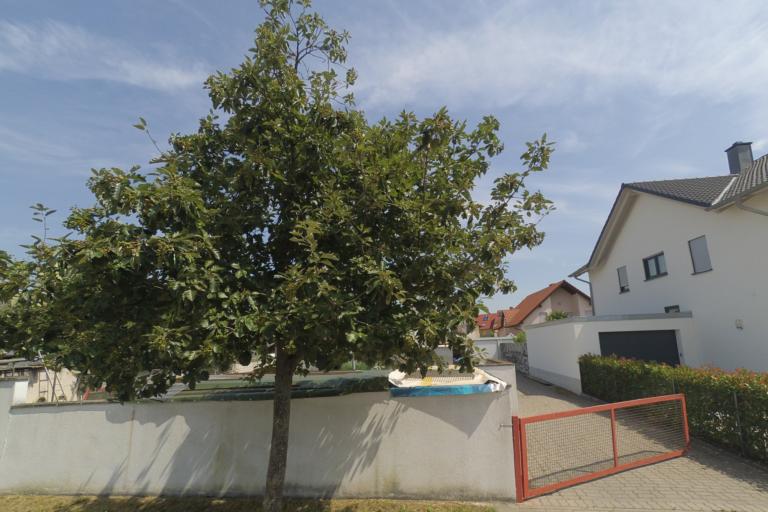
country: DE
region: Rheinland-Pfalz
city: Schifferstadt
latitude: 49.3879
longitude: 8.3815
